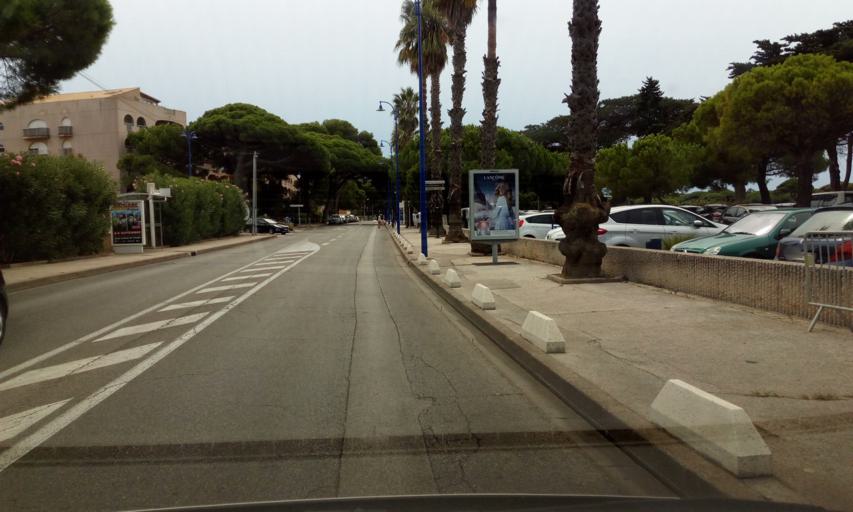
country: FR
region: Provence-Alpes-Cote d'Azur
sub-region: Departement du Var
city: Hyeres
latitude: 43.0817
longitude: 6.1538
